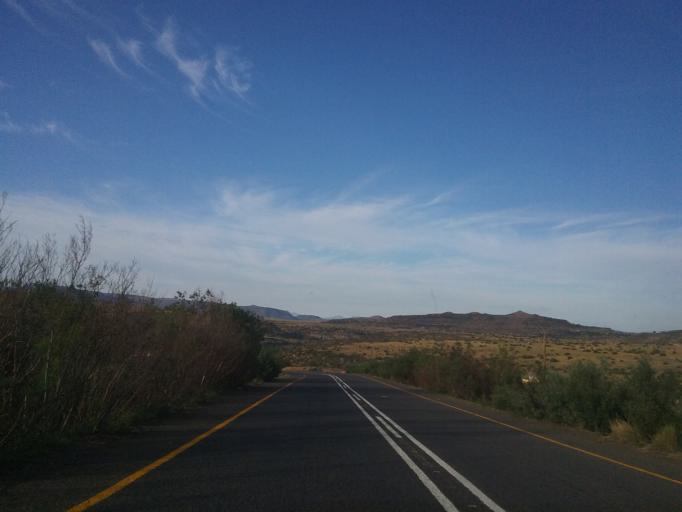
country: LS
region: Mohale's Hoek District
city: Mohale's Hoek
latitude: -30.2758
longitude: 27.4545
